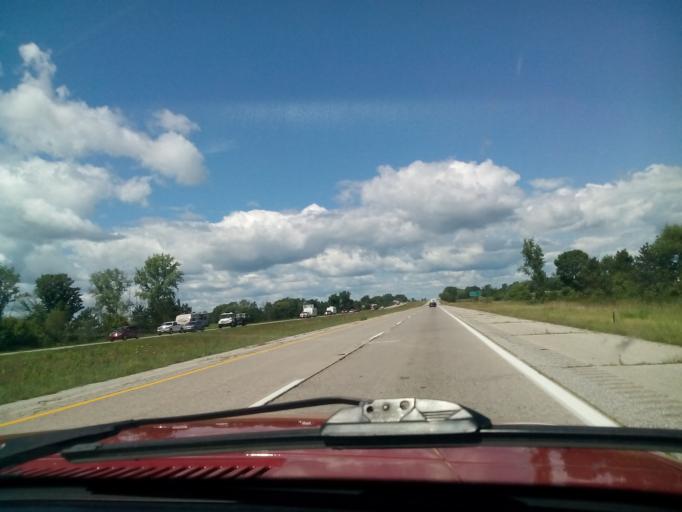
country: US
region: Michigan
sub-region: Bay County
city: Bay City
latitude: 43.6322
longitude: -83.9646
